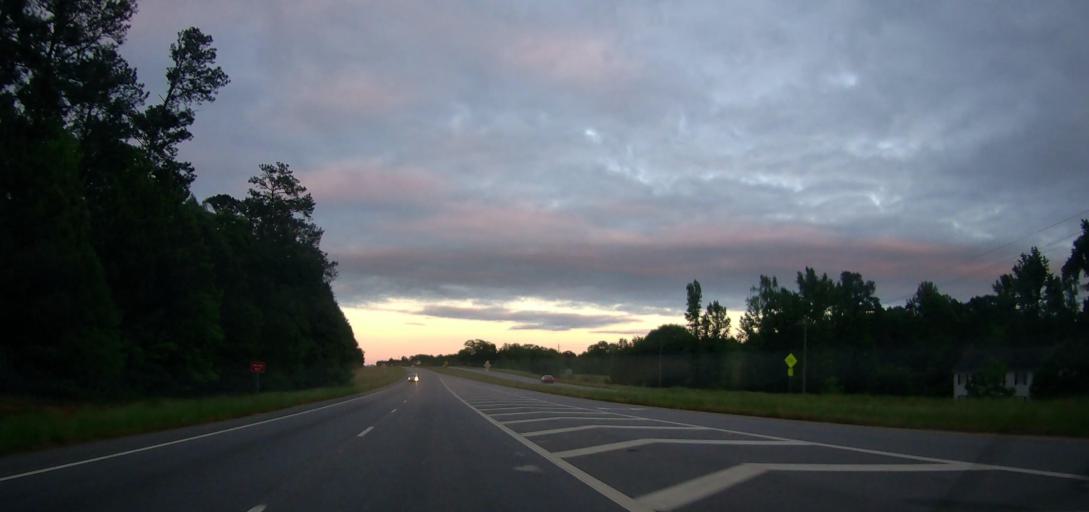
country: US
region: Georgia
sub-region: Clarke County
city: Country Club Estates
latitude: 34.0110
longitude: -83.4778
